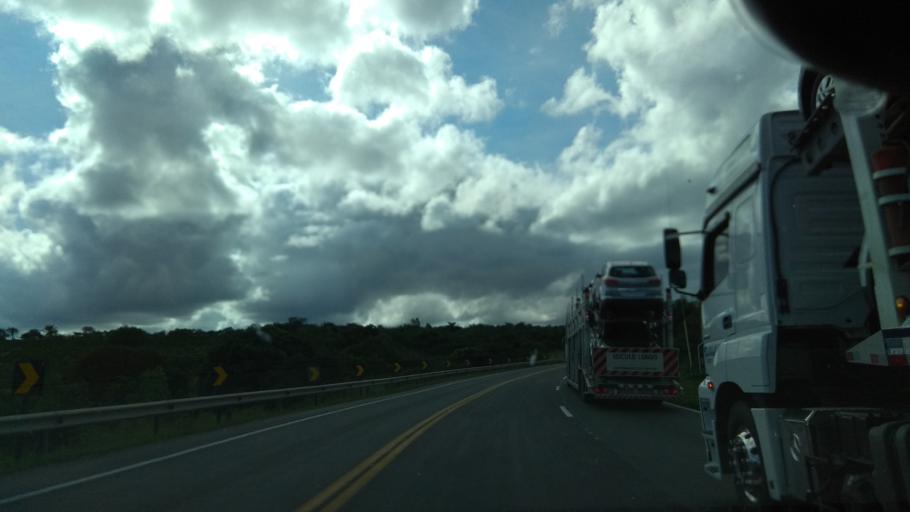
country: BR
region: Bahia
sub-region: Santa Ines
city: Santa Ines
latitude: -13.1076
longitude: -39.9955
